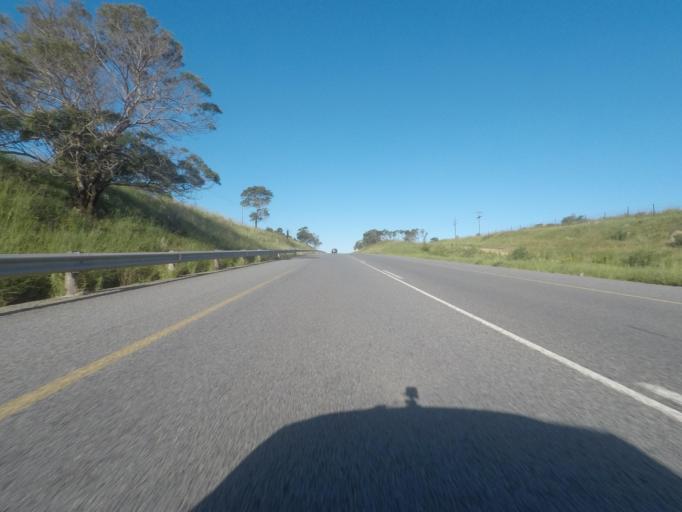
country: ZA
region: Eastern Cape
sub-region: Buffalo City Metropolitan Municipality
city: East London
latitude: -33.0583
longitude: 27.7948
